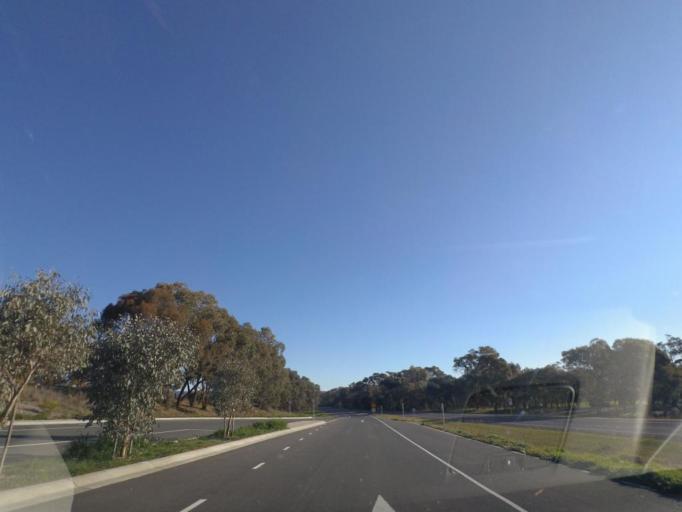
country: AU
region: Victoria
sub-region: Greater Shepparton
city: Shepparton
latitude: -36.7820
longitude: 145.5000
